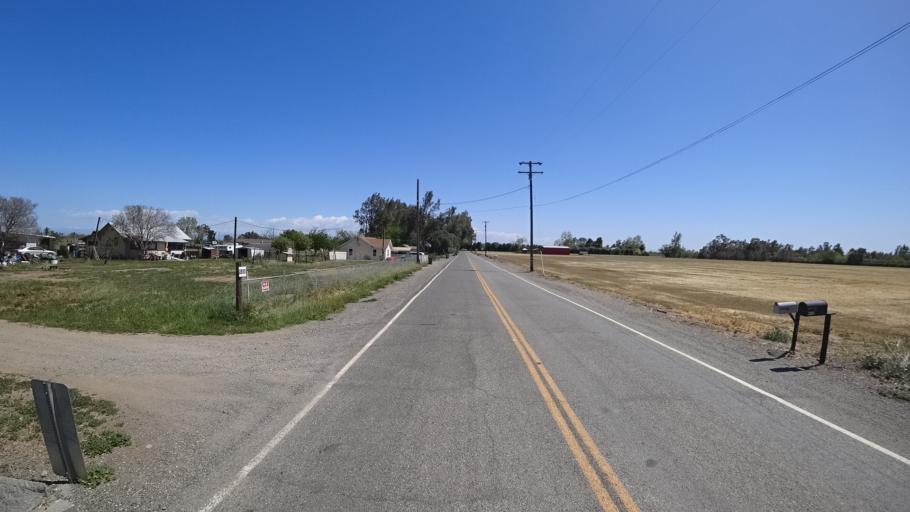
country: US
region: California
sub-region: Glenn County
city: Orland
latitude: 39.7837
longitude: -122.2015
